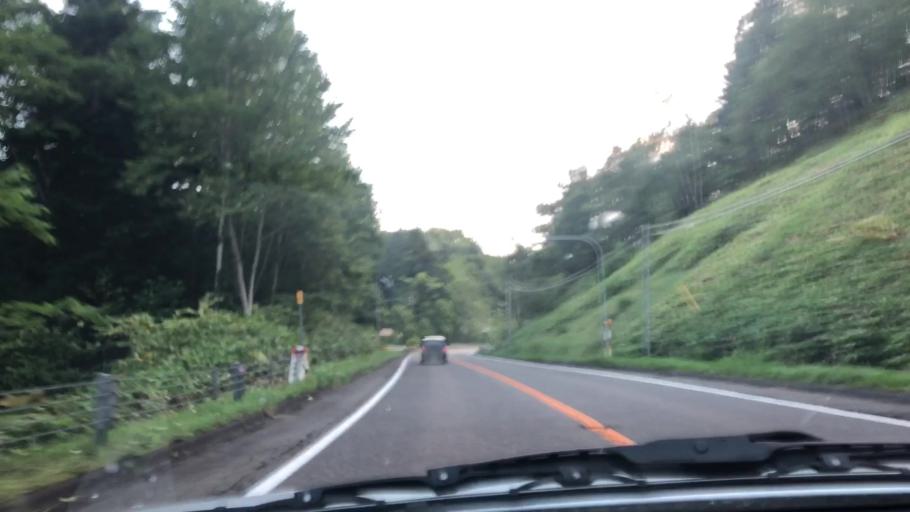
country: JP
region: Hokkaido
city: Shimo-furano
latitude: 42.8797
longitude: 142.2298
